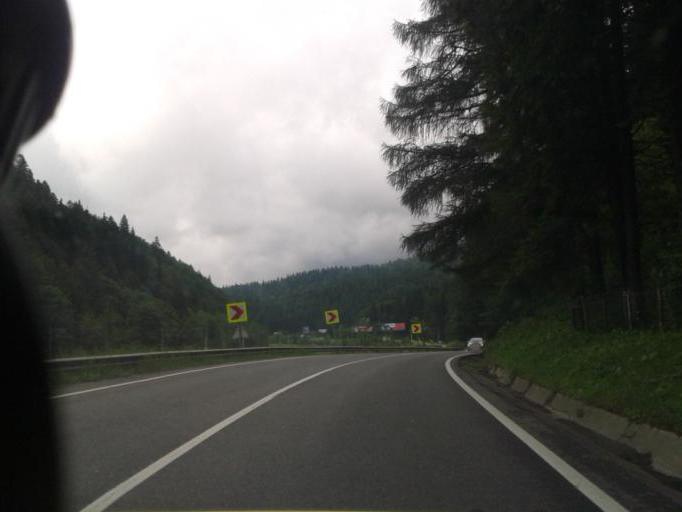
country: RO
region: Prahova
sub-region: Oras Azuga
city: Azuga
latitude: 45.4518
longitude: 25.5635
